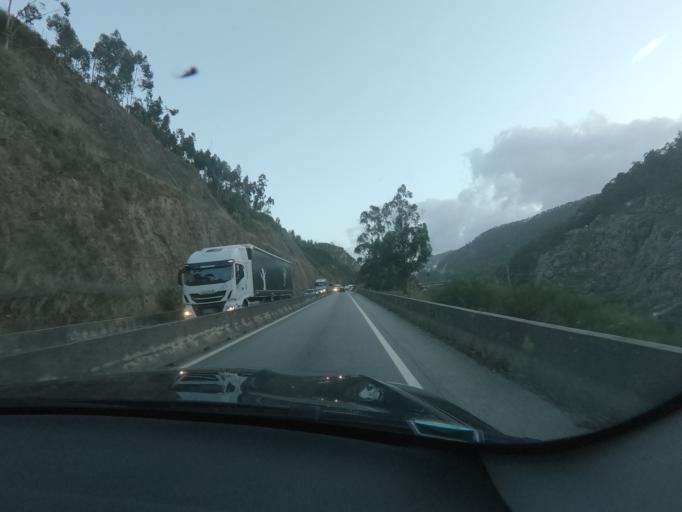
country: PT
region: Coimbra
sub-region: Penacova
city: Penacova
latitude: 40.2850
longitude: -8.2625
